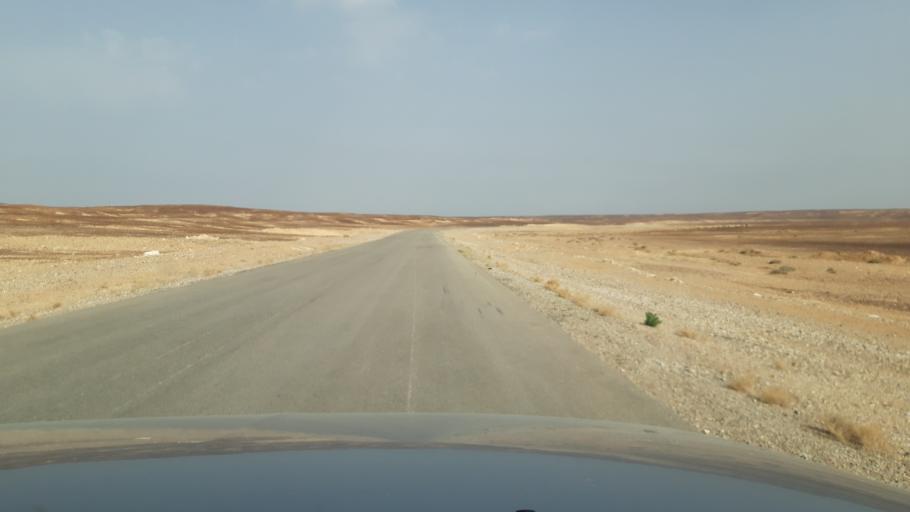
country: JO
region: Amman
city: Al Azraq ash Shamali
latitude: 31.2772
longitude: 36.5841
